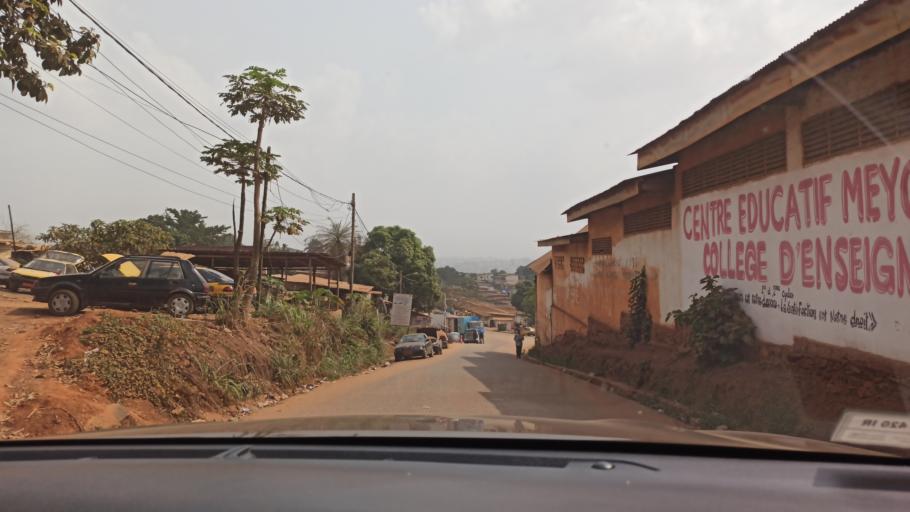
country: CM
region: Centre
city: Yaounde
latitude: 3.8766
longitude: 11.4830
